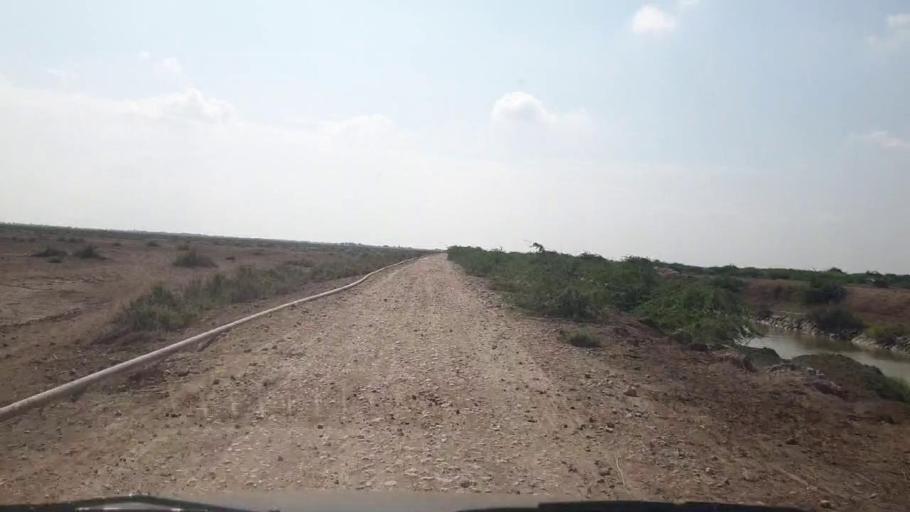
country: PK
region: Sindh
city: Badin
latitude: 24.5064
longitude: 68.6081
